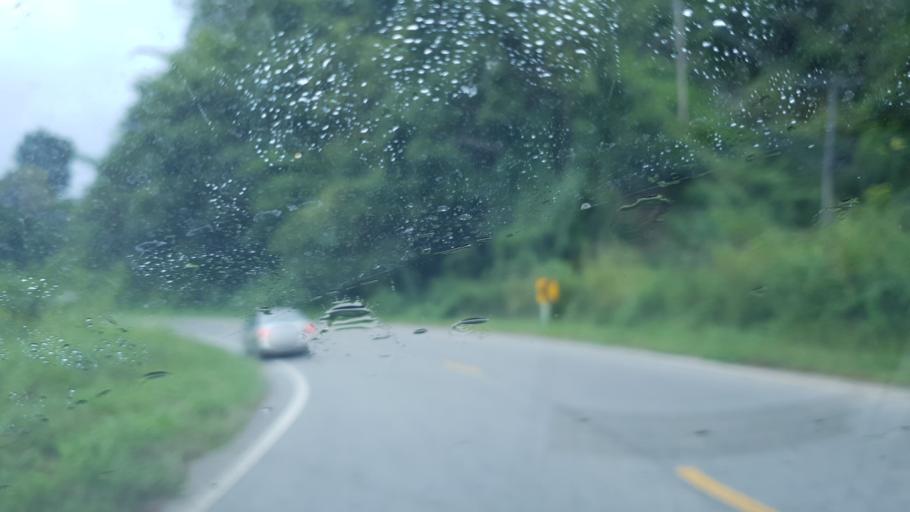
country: TH
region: Mae Hong Son
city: Khun Yuam
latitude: 18.7047
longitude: 97.9137
